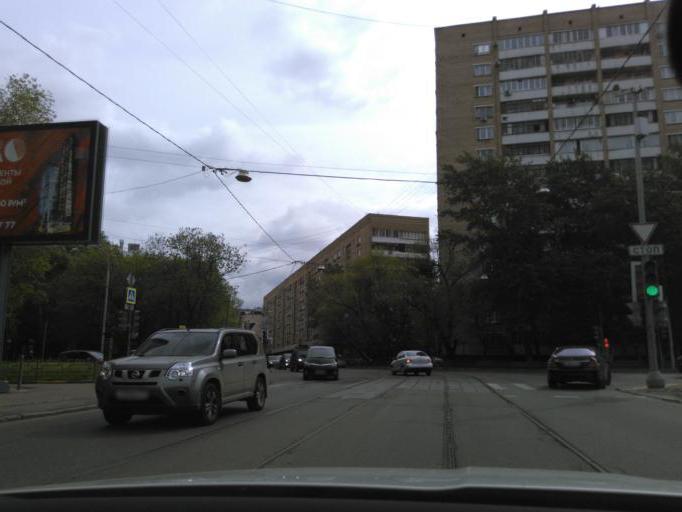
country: RU
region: Moscow
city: Mar'ina Roshcha
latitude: 55.7889
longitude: 37.6285
